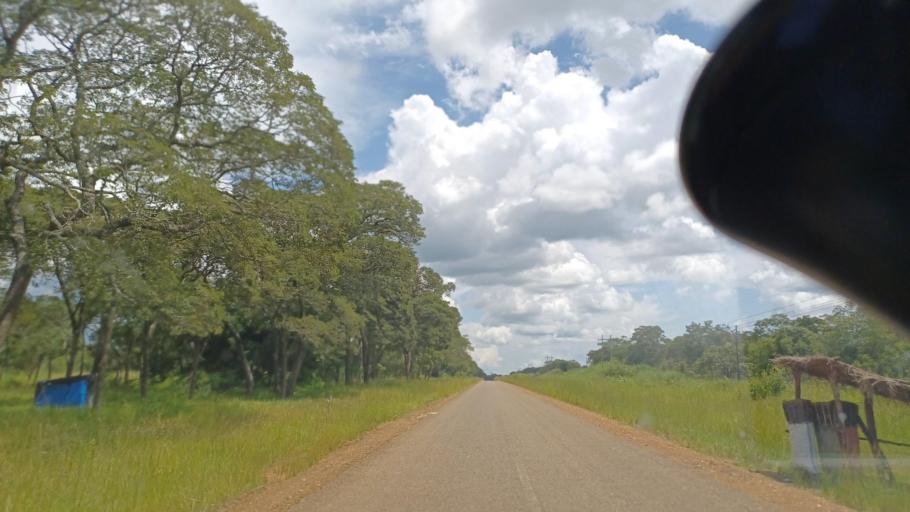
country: ZM
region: North-Western
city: Solwezi
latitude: -12.7077
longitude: 26.0293
